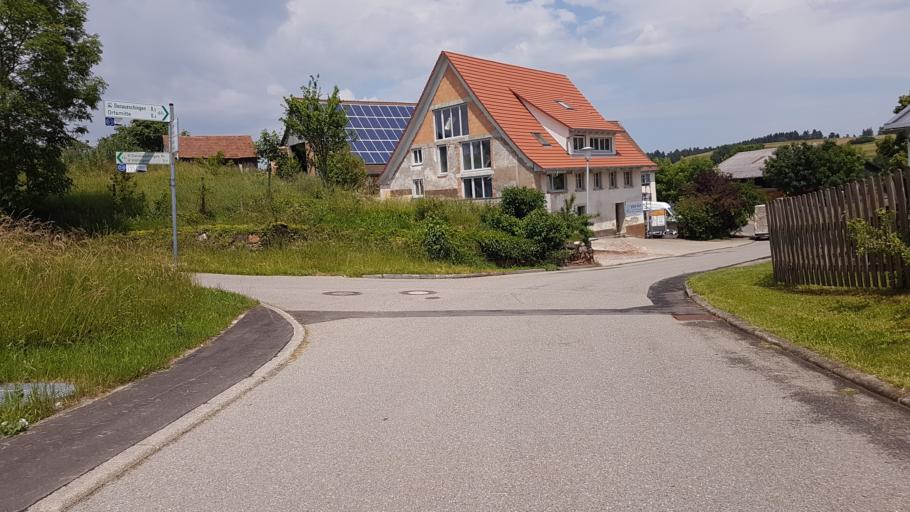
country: DE
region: Baden-Wuerttemberg
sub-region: Freiburg Region
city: Hufingen
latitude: 47.8933
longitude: 8.4863
